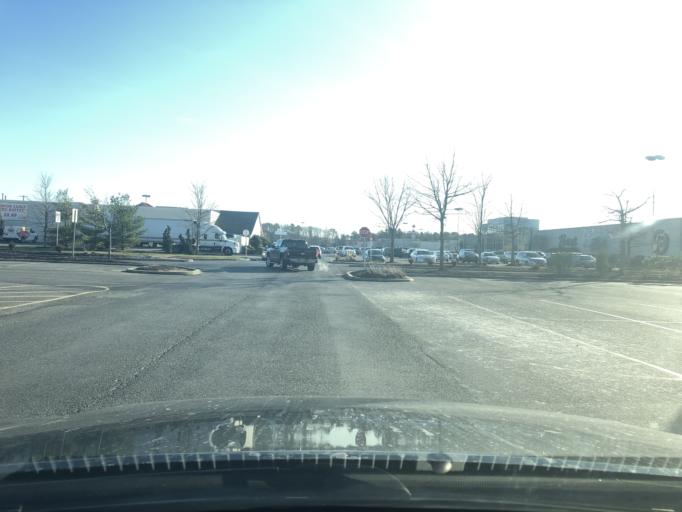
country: US
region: New Jersey
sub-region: Atlantic County
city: Northfield
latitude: 39.4019
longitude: -74.5631
